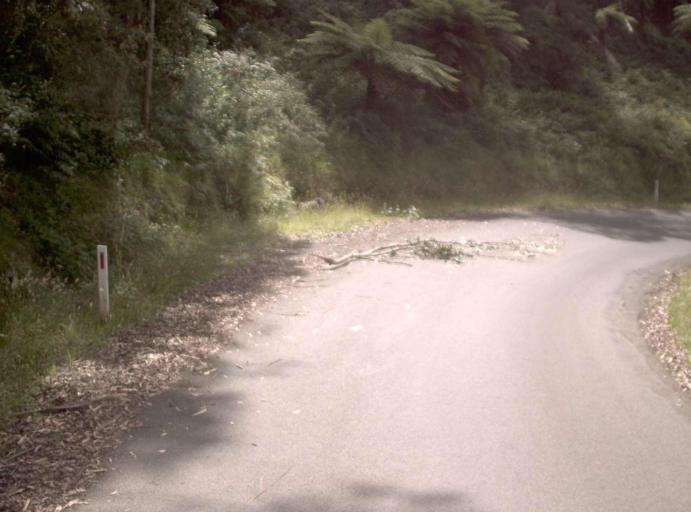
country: AU
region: Victoria
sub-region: Latrobe
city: Moe
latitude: -37.8321
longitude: 146.1873
